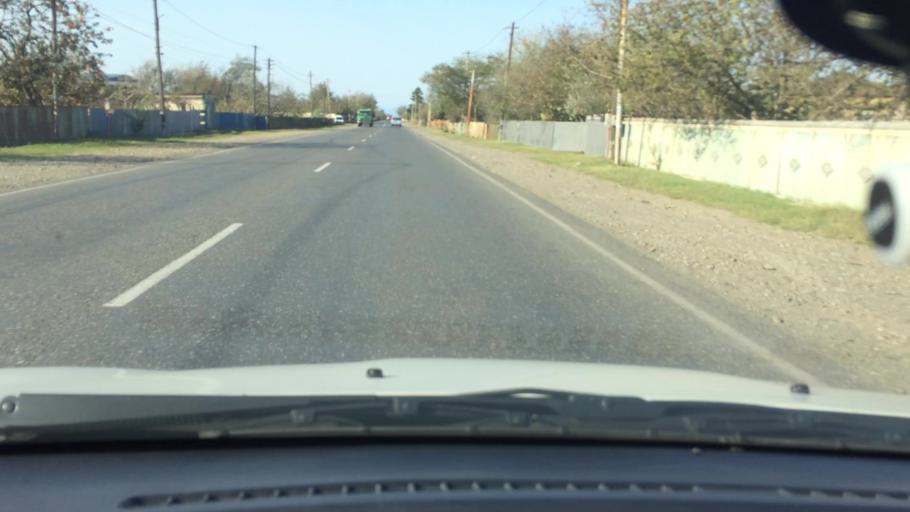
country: GE
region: Imereti
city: Kutaisi
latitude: 42.2414
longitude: 42.6296
